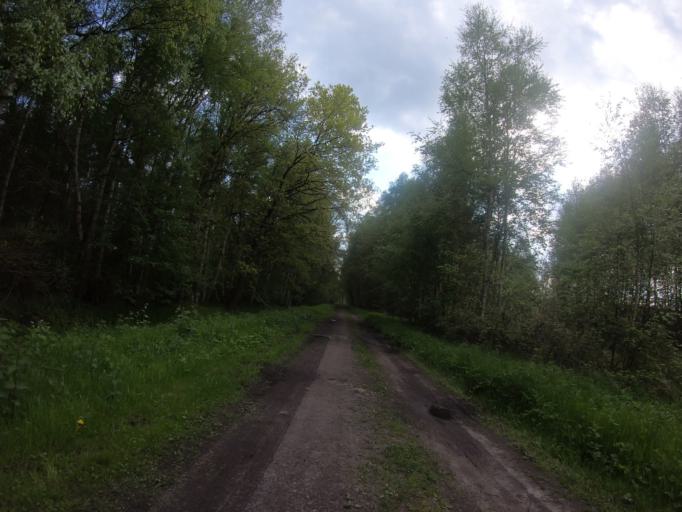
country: DE
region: Lower Saxony
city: Sassenburg
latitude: 52.5126
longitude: 10.6163
